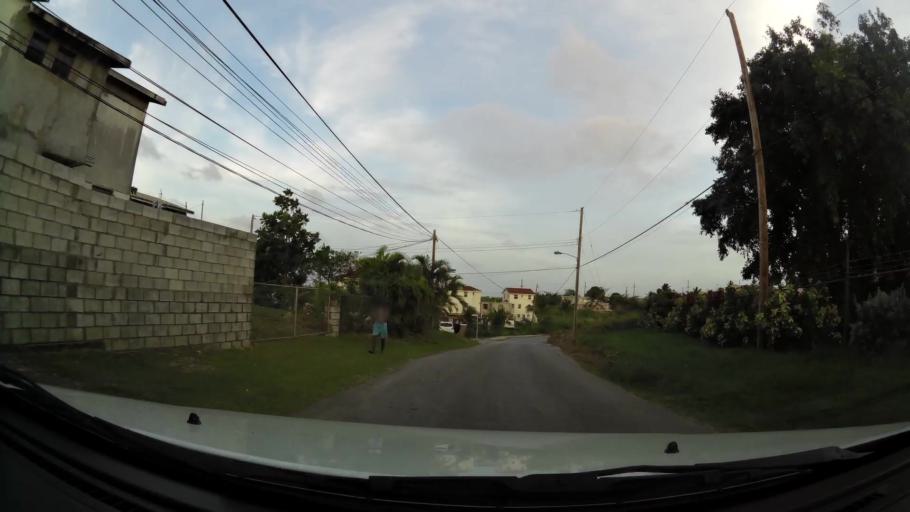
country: BB
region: Saint Philip
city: Crane
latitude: 13.0973
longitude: -59.4948
